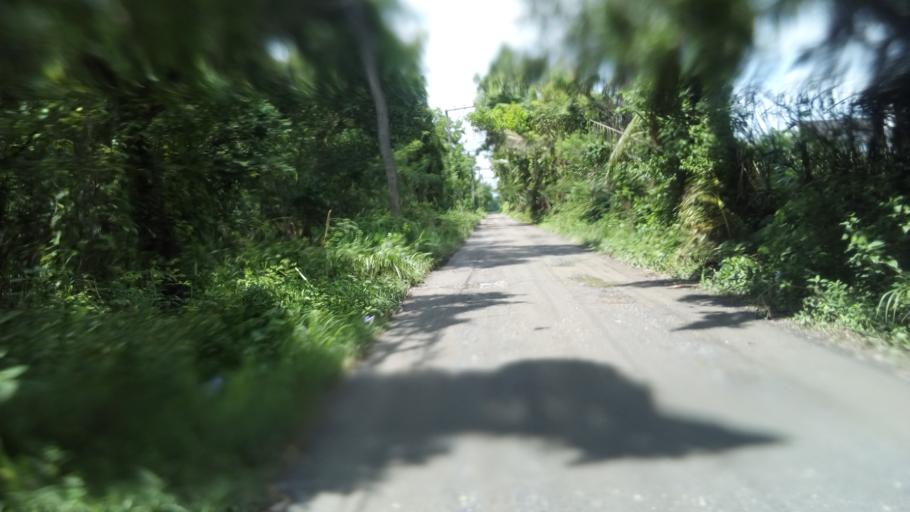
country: TH
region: Pathum Thani
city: Nong Suea
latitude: 14.0601
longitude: 100.8576
